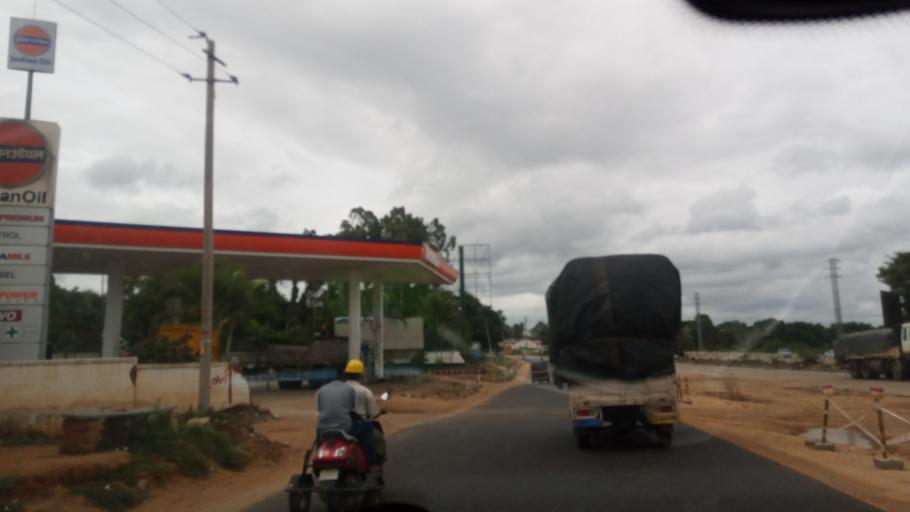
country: IN
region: Karnataka
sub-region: Mandya
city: Shrirangapattana
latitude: 12.3719
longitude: 76.6634
